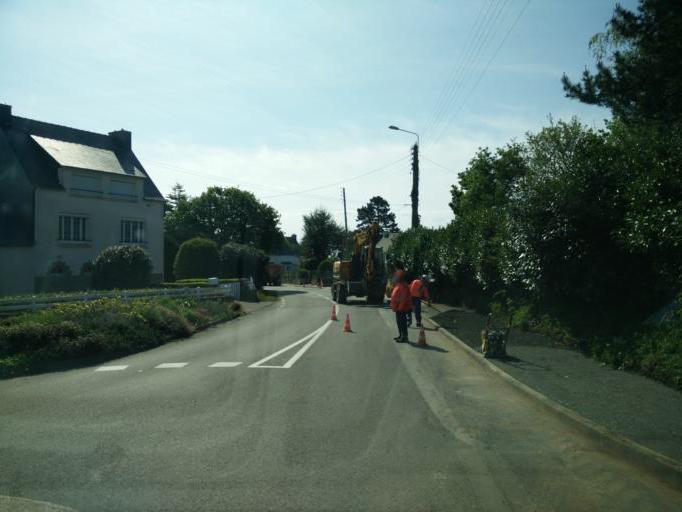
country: FR
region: Brittany
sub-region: Departement du Finistere
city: Crozon
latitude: 48.2427
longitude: -4.4784
